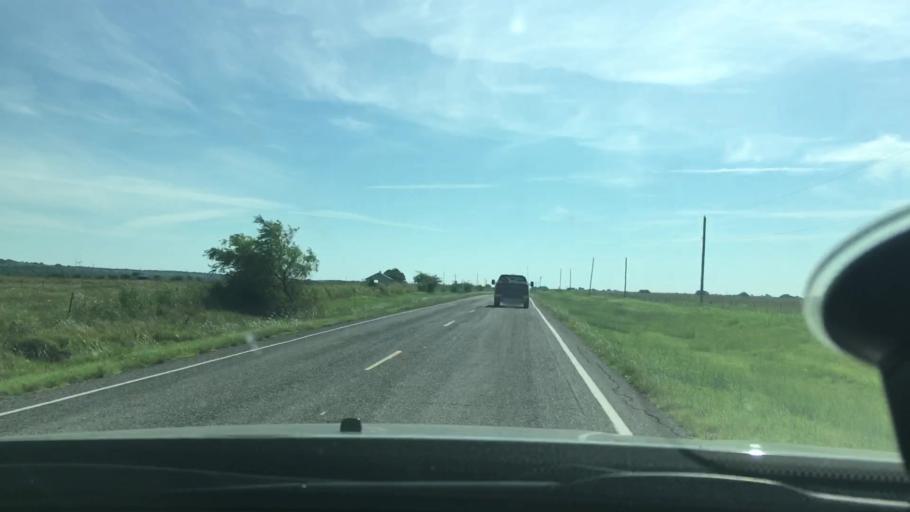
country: US
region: Oklahoma
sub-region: Carter County
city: Lone Grove
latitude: 34.3327
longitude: -97.2562
